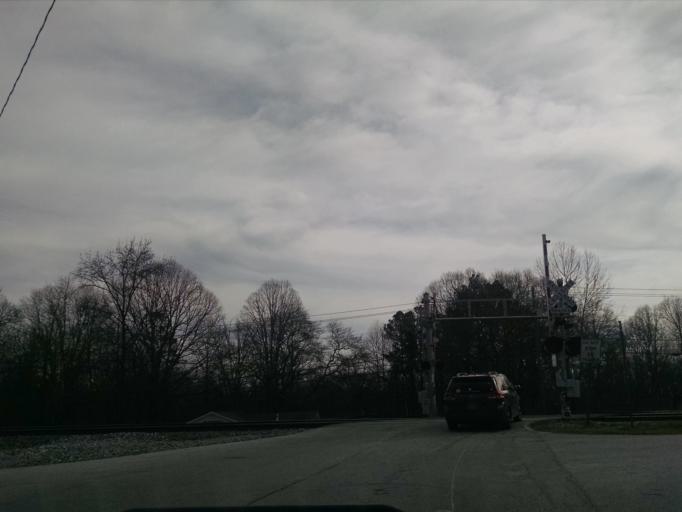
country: US
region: Georgia
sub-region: Gwinnett County
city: Sugar Hill
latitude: 34.1009
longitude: -84.0299
